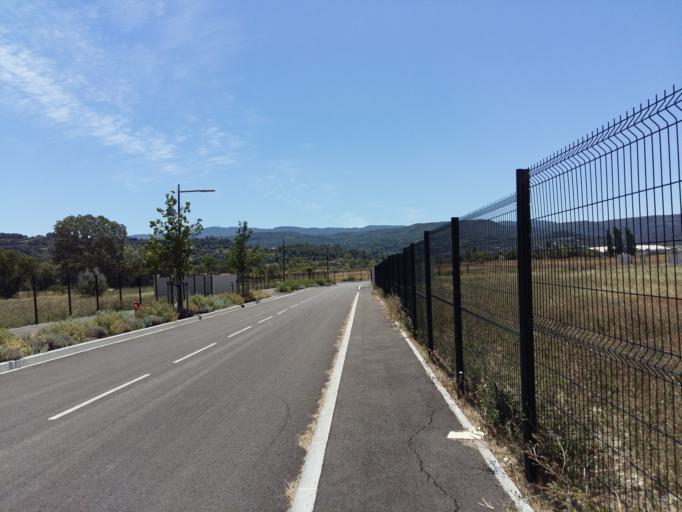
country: FR
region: Provence-Alpes-Cote d'Azur
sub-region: Departement du Vaucluse
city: Gargas
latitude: 43.8960
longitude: 5.3756
